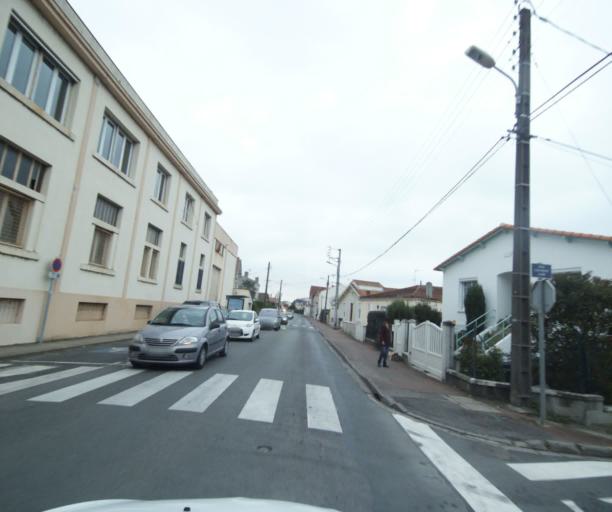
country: FR
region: Poitou-Charentes
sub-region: Departement de la Charente-Maritime
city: Saintes
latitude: 45.7389
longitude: -0.6178
